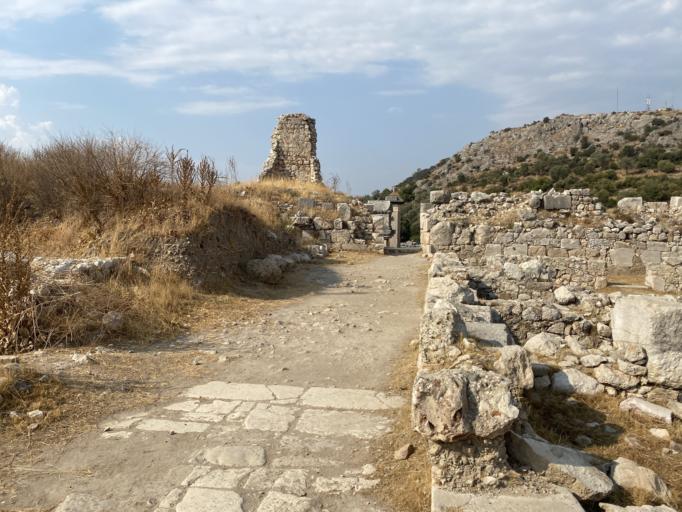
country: TR
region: Mugla
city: Esen
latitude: 36.3562
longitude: 29.3179
